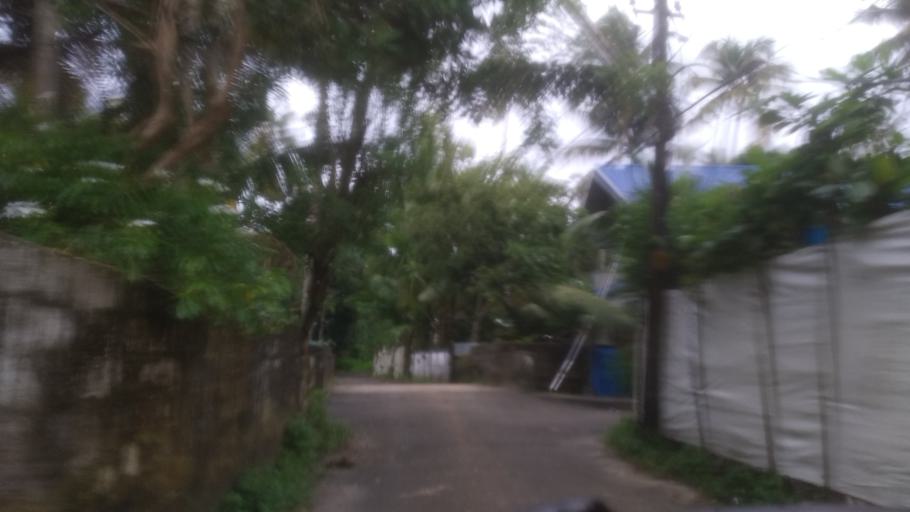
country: IN
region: Kerala
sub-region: Ernakulam
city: Elur
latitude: 10.0839
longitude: 76.2049
